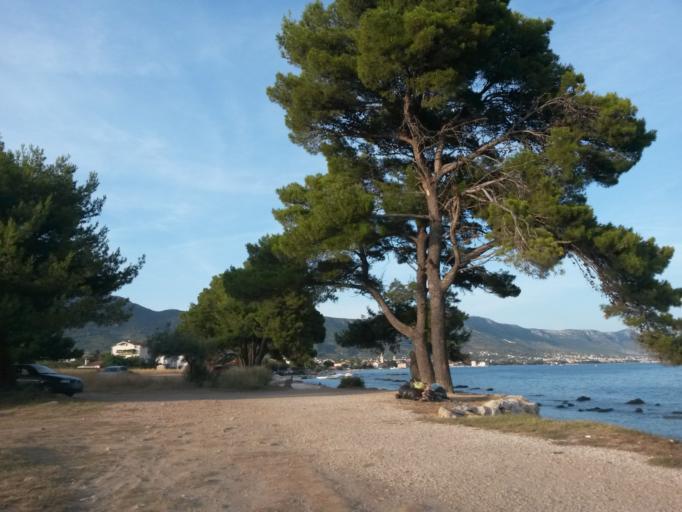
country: HR
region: Splitsko-Dalmatinska
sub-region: Grad Trogir
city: Trogir
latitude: 43.5424
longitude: 16.3215
